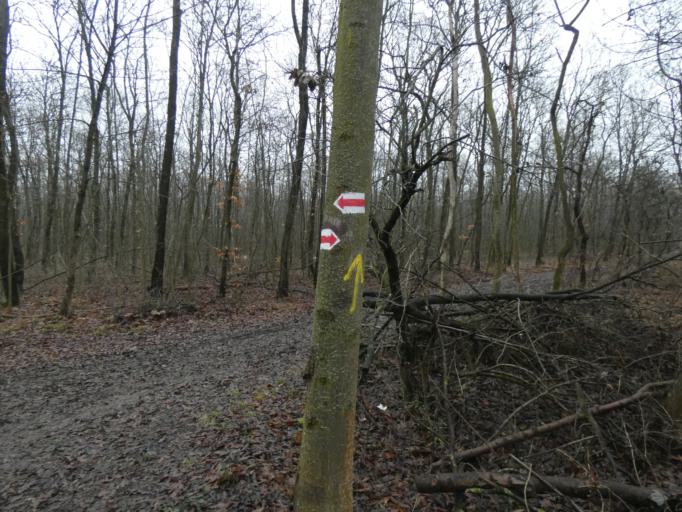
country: HU
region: Pest
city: Soskut
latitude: 47.4391
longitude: 18.8443
